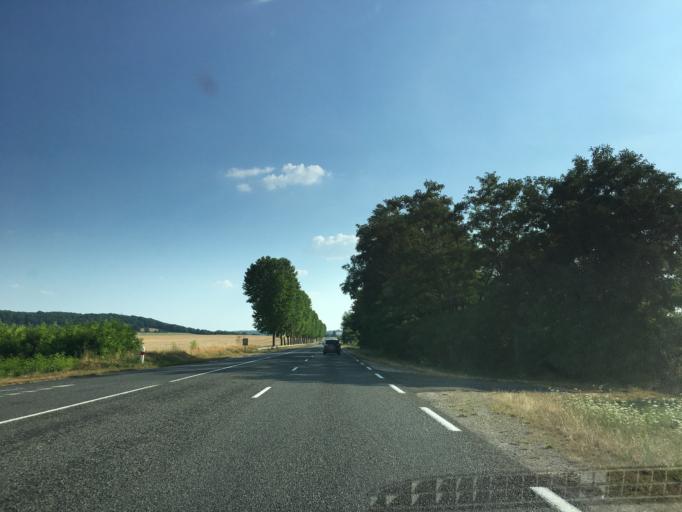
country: FR
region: Bourgogne
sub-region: Departement de l'Yonne
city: Veron
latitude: 48.1196
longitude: 3.2913
